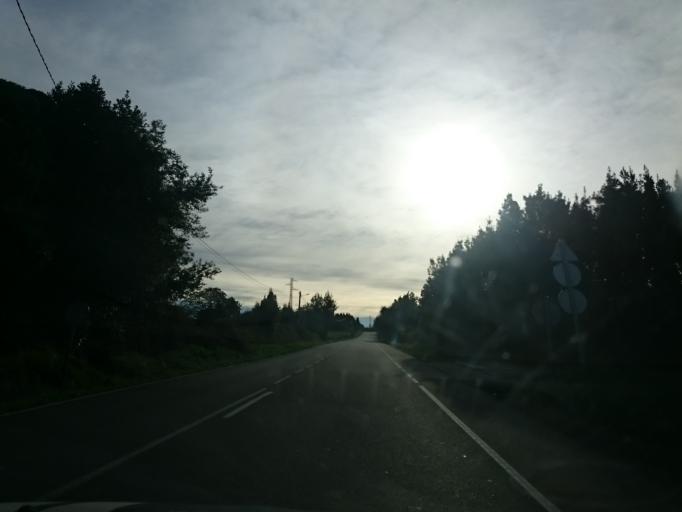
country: ES
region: Asturias
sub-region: Province of Asturias
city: Arriba
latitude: 43.5146
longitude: -5.5977
